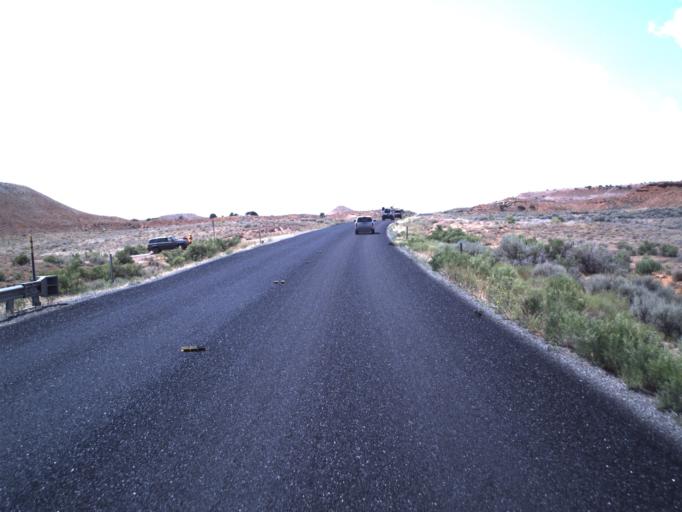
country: US
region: Utah
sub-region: Uintah County
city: Maeser
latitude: 40.4119
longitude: -109.7327
